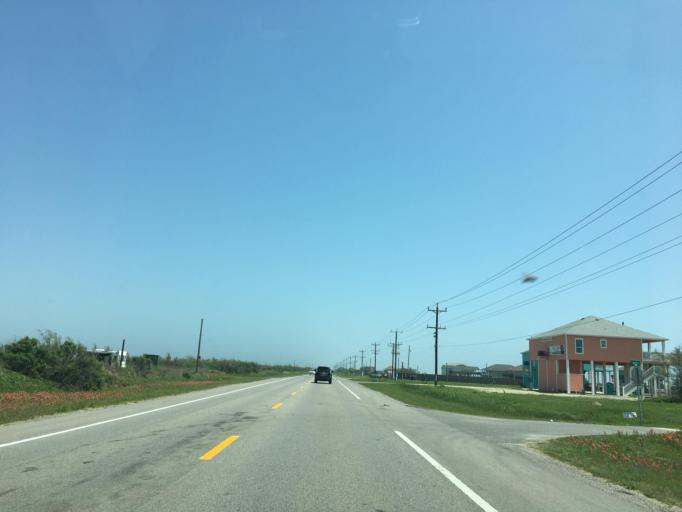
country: US
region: Texas
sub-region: Galveston County
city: Bolivar Peninsula
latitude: 29.4941
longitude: -94.5392
